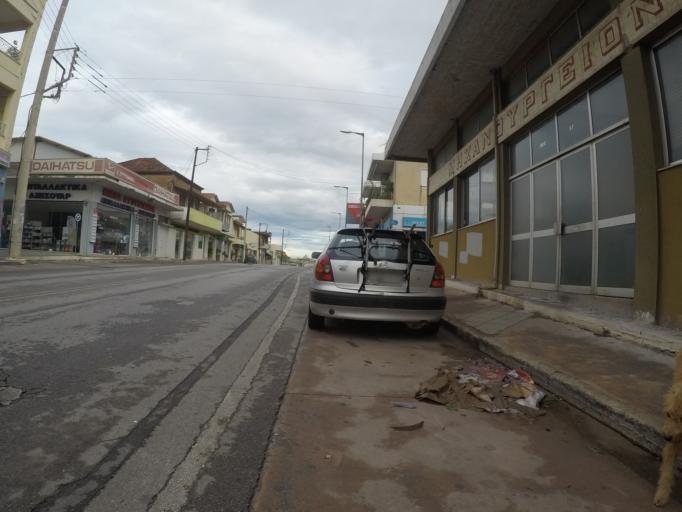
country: GR
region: Peloponnese
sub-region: Nomos Messinias
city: Kalamata
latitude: 37.0411
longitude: 22.1003
